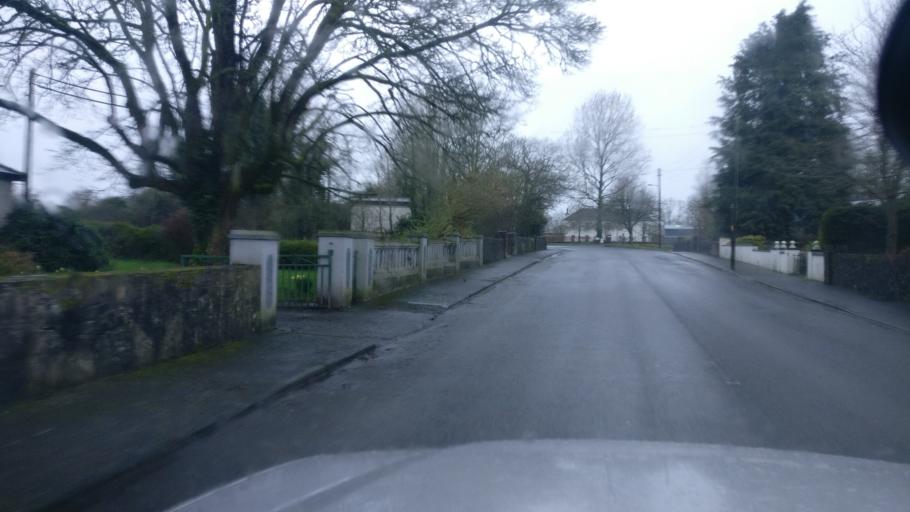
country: IE
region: Connaught
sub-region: County Galway
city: Ballinasloe
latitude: 53.2365
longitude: -8.1781
